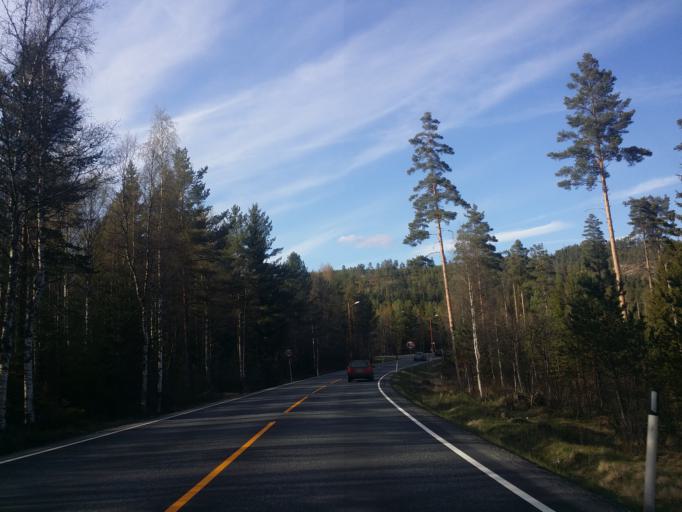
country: NO
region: Buskerud
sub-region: Kongsberg
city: Kongsberg
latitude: 59.6246
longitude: 9.4735
